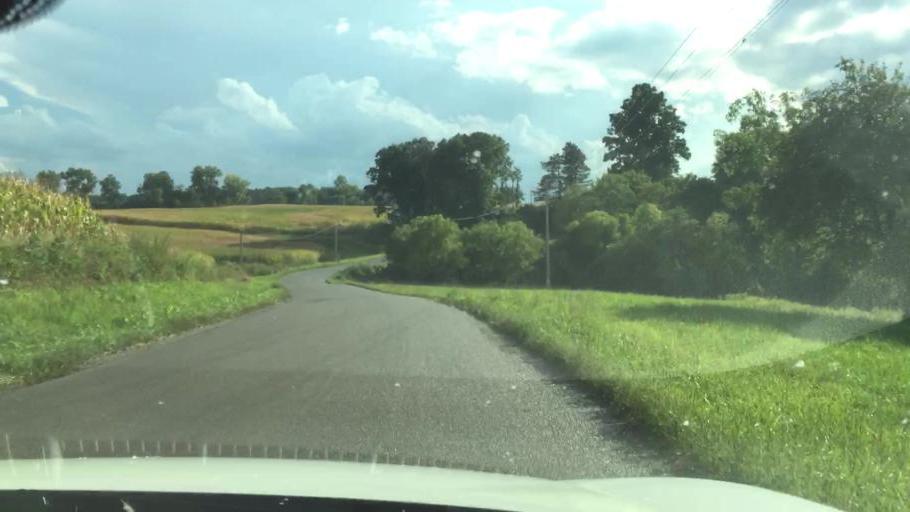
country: US
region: Ohio
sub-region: Champaign County
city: Mechanicsburg
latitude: 40.0322
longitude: -83.6042
